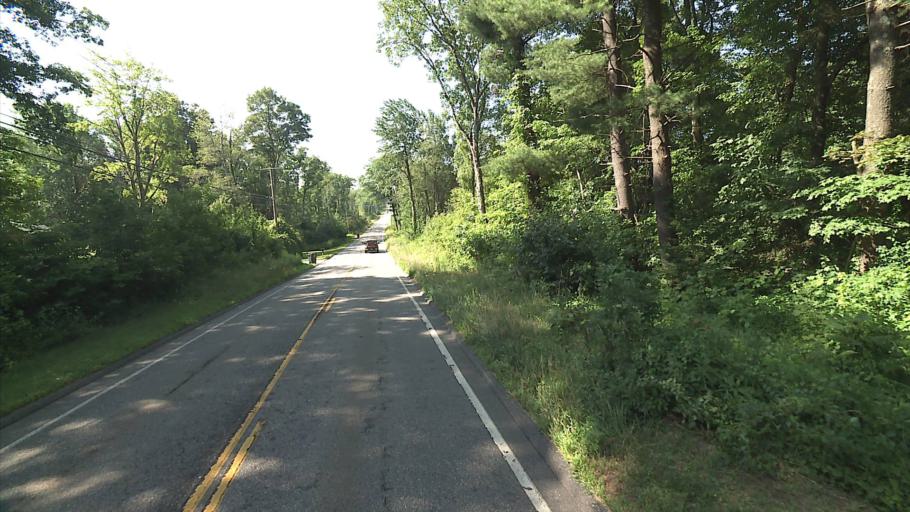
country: US
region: Connecticut
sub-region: Litchfield County
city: Torrington
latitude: 41.8443
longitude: -73.0749
